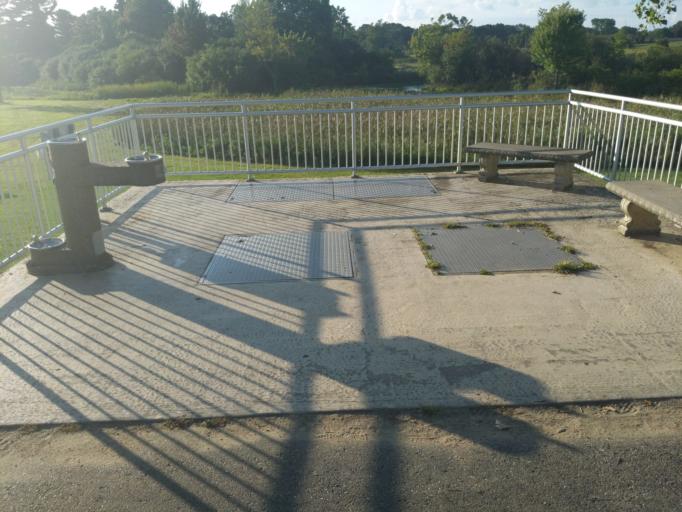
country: US
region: Michigan
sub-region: Jackson County
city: Jackson
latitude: 42.2281
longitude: -84.4281
